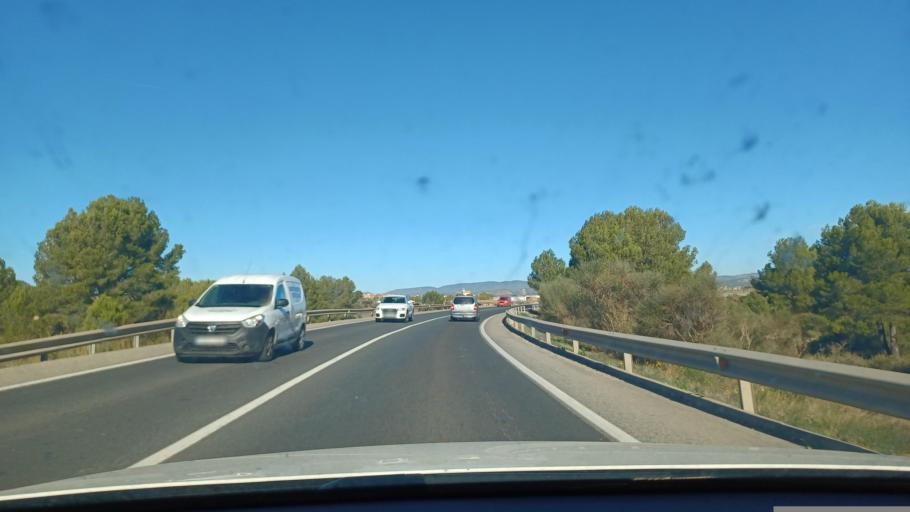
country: ES
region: Catalonia
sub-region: Provincia de Tarragona
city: Montblanc
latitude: 41.3631
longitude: 1.1752
